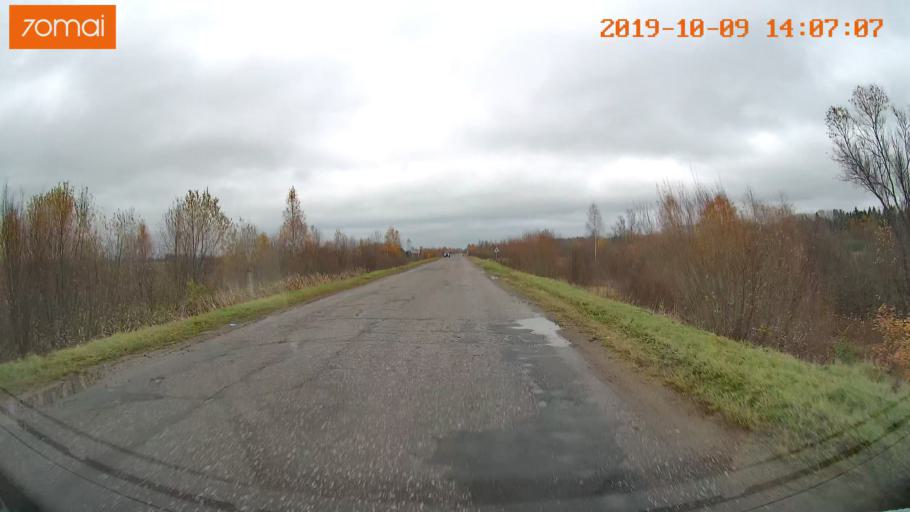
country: RU
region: Kostroma
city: Buy
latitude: 58.4684
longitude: 41.4179
